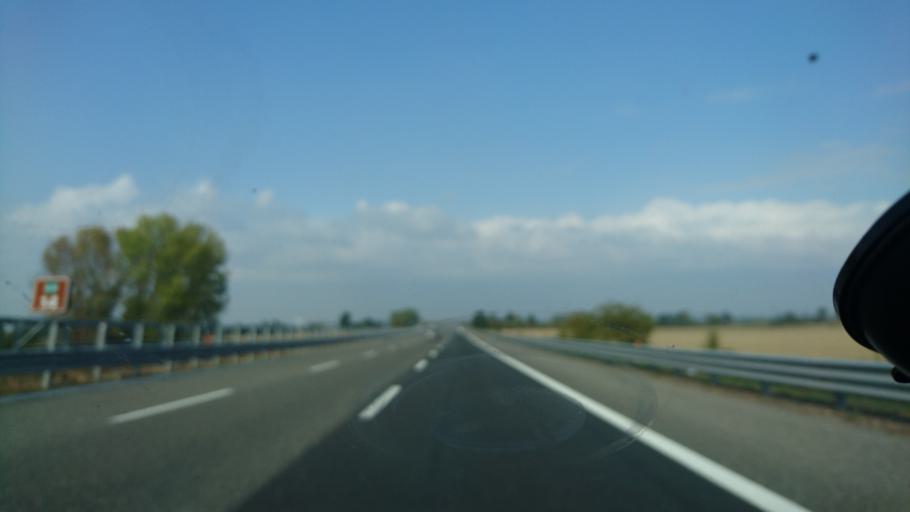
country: IT
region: Piedmont
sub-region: Provincia di Alessandria
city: Castellazzo Bormida
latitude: 44.8825
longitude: 8.5695
